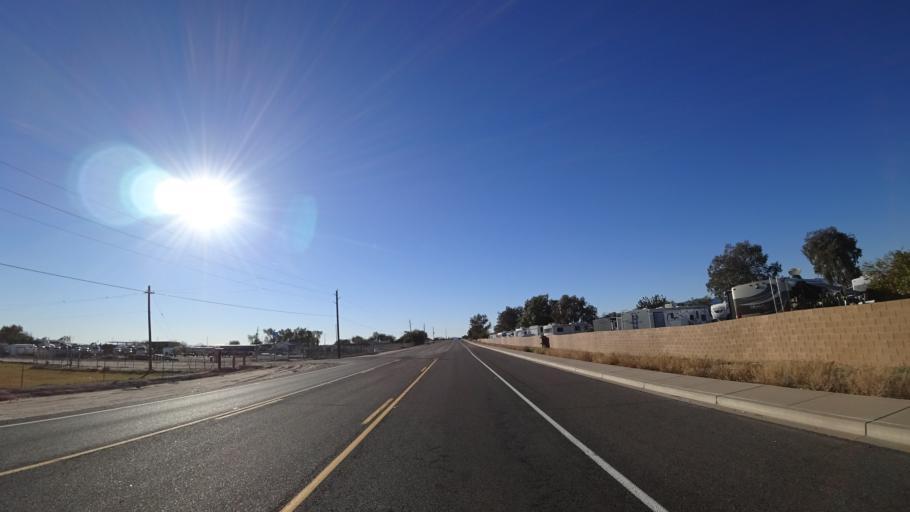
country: US
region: Arizona
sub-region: Maricopa County
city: Goodyear
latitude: 33.4502
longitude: -112.4480
